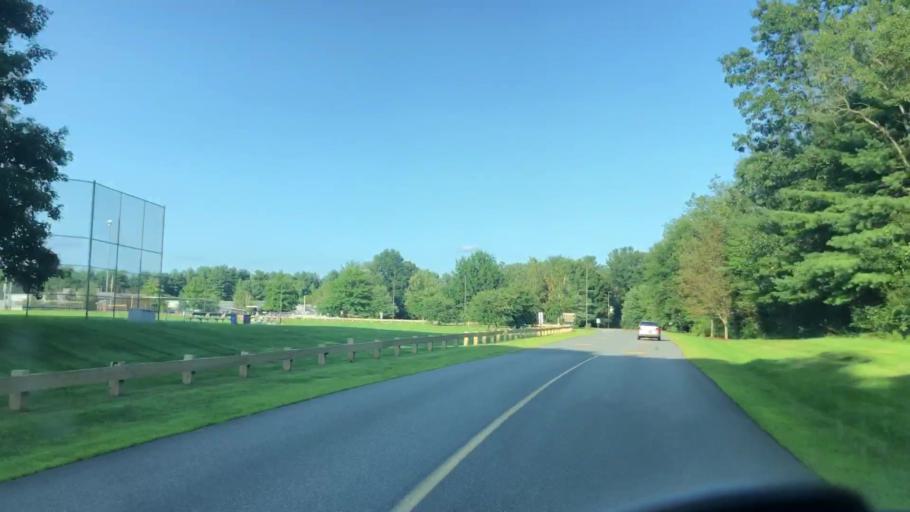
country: US
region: Massachusetts
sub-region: Franklin County
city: Northfield
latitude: 42.6814
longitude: -72.4880
